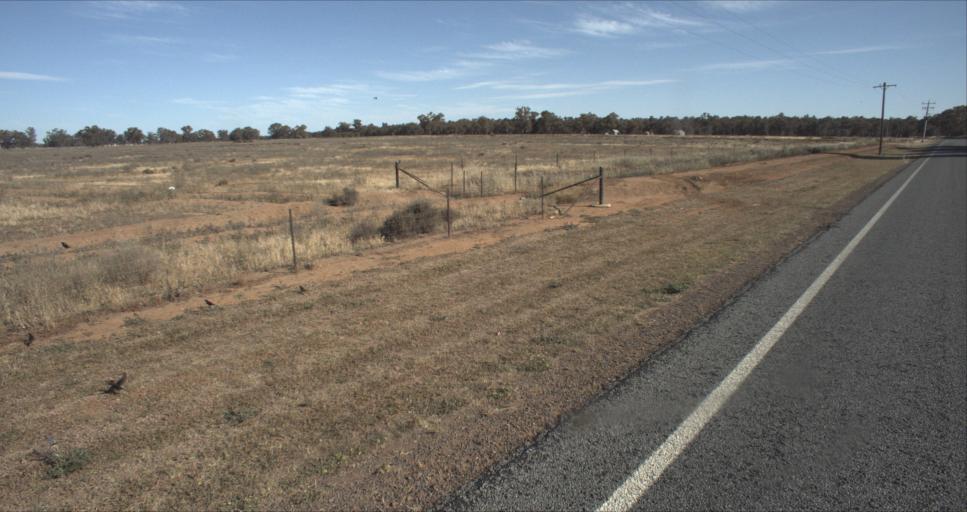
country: AU
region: New South Wales
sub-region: Leeton
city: Leeton
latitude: -34.6200
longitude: 146.3978
